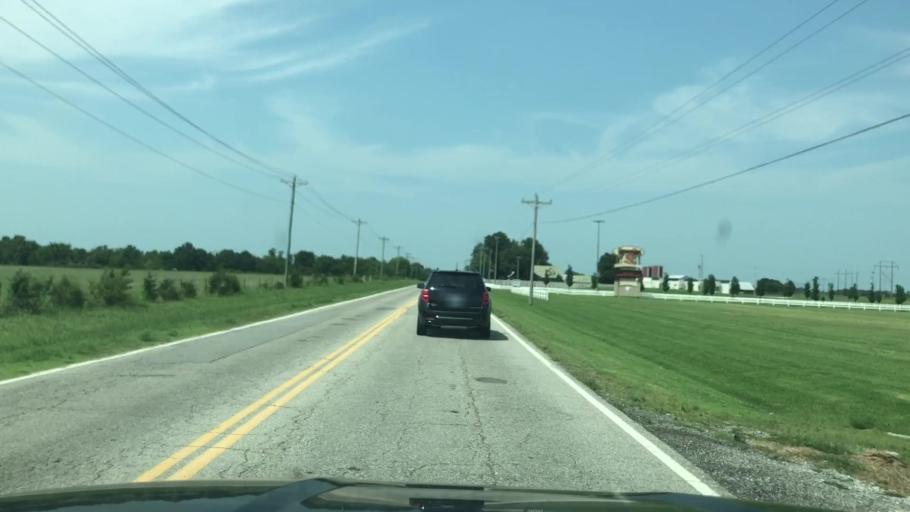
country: US
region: Oklahoma
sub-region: Ottawa County
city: Miami
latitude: 36.8902
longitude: -94.8418
